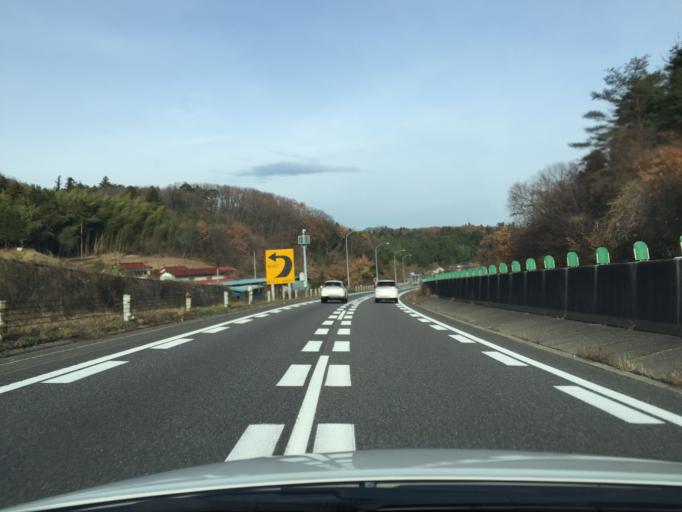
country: JP
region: Fukushima
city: Nihommatsu
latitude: 37.6288
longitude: 140.4320
